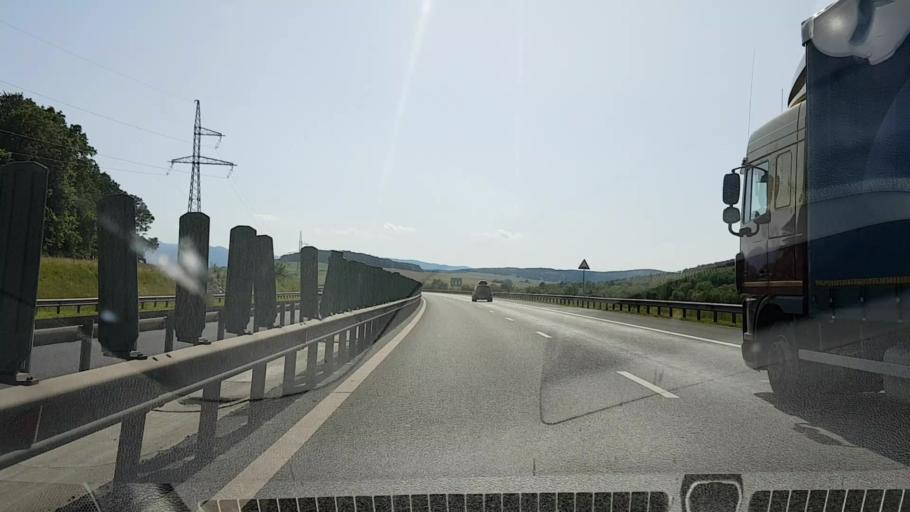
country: RO
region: Sibiu
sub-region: Comuna Cristian
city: Cristian
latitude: 45.8029
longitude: 24.0402
